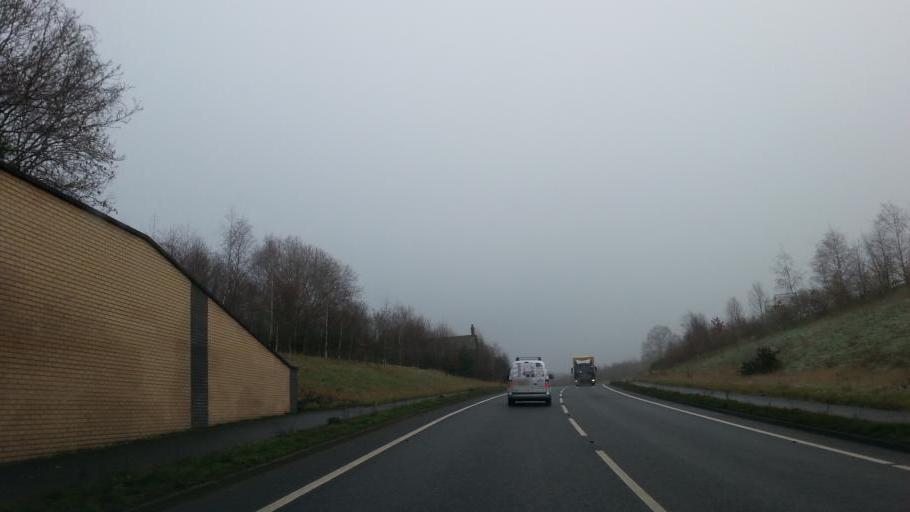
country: GB
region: England
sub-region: Cheshire East
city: Alderley Edge
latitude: 53.3075
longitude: -2.2439
